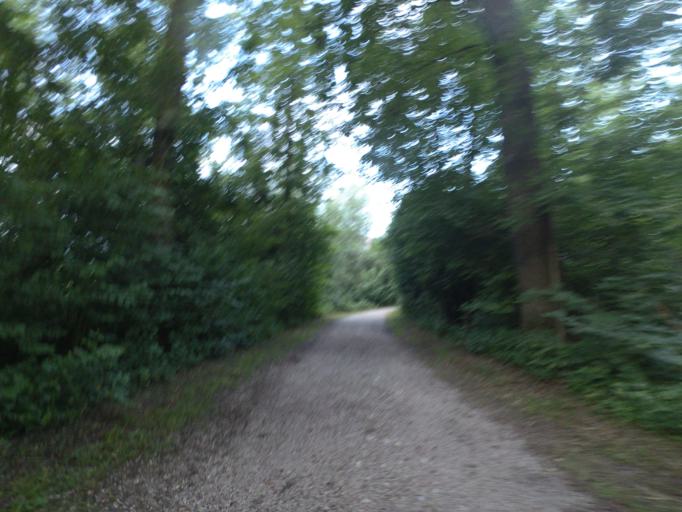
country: AT
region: Salzburg
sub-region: Politischer Bezirk Hallein
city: Puch bei Hallein
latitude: 47.7102
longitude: 13.0842
